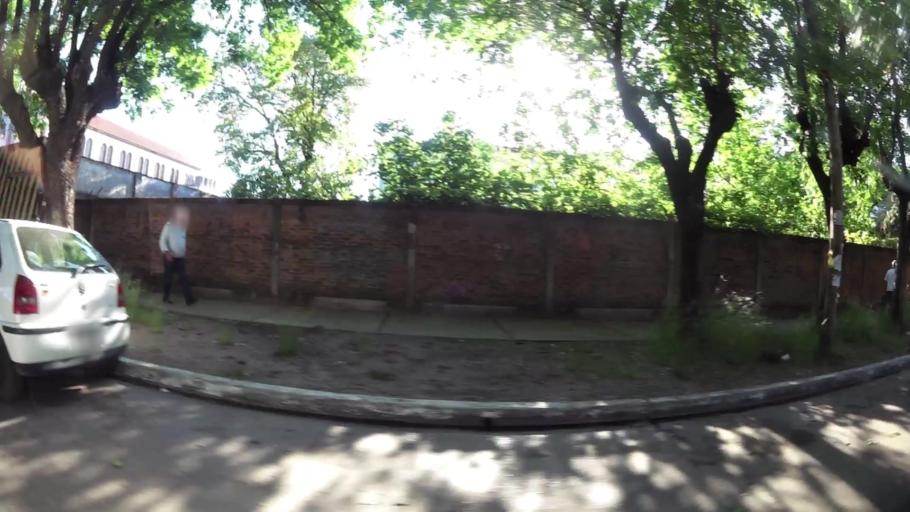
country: AR
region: Buenos Aires
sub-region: Partido de Merlo
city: Merlo
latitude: -34.6711
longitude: -58.7260
